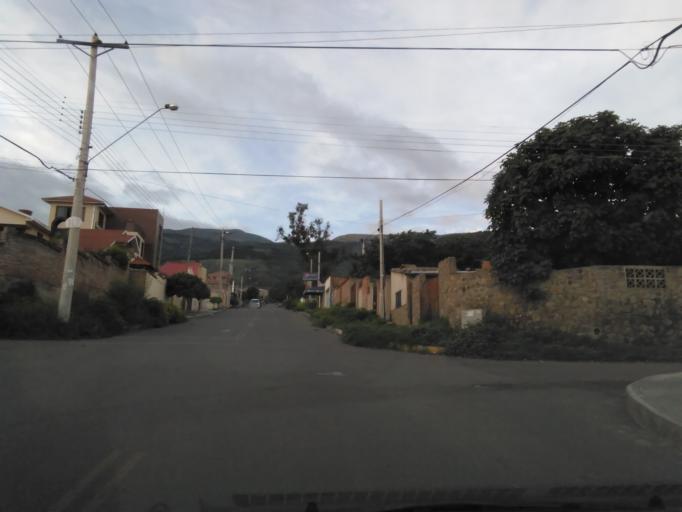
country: BO
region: Cochabamba
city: Cochabamba
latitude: -17.3594
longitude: -66.1559
